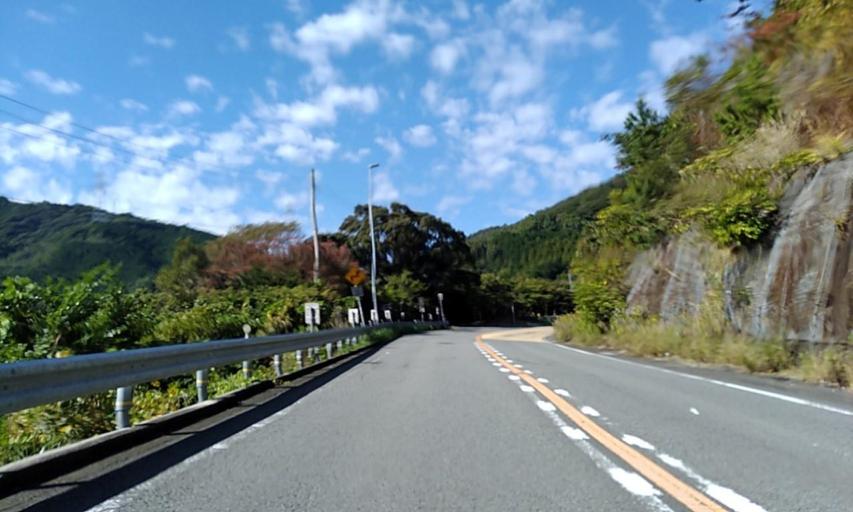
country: JP
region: Wakayama
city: Gobo
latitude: 33.9907
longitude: 135.1868
